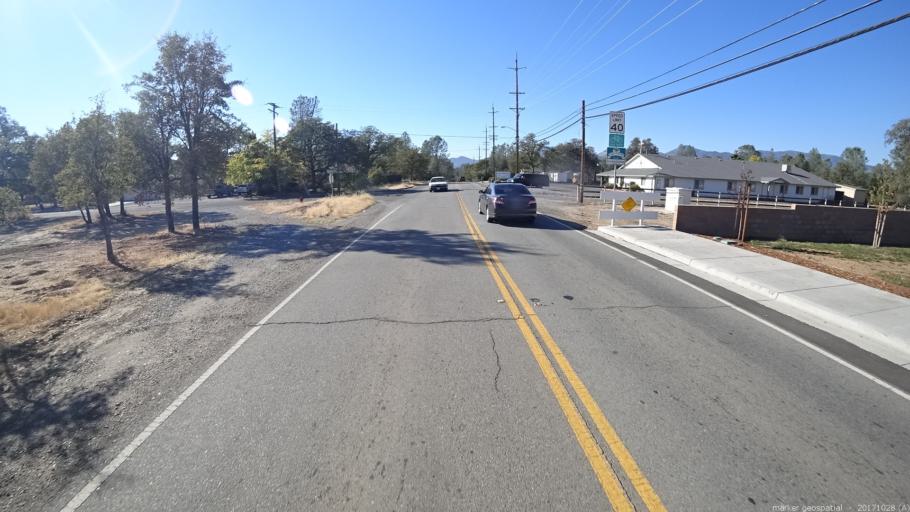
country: US
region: California
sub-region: Shasta County
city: Redding
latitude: 40.6256
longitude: -122.4064
